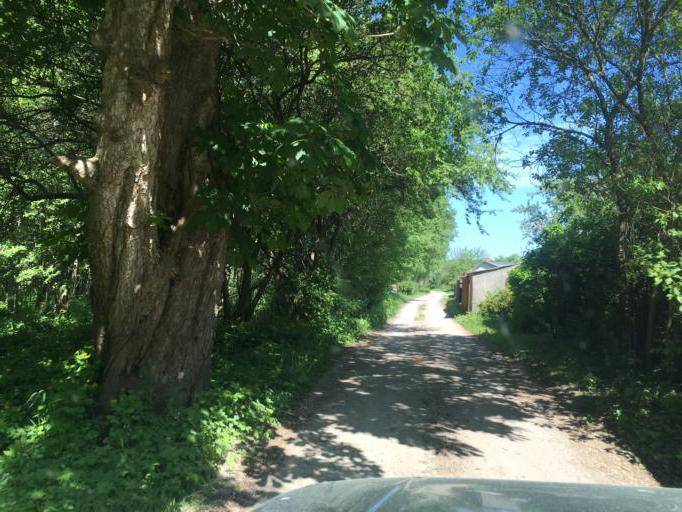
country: LV
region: Ventspils
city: Ventspils
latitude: 57.4541
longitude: 21.6533
